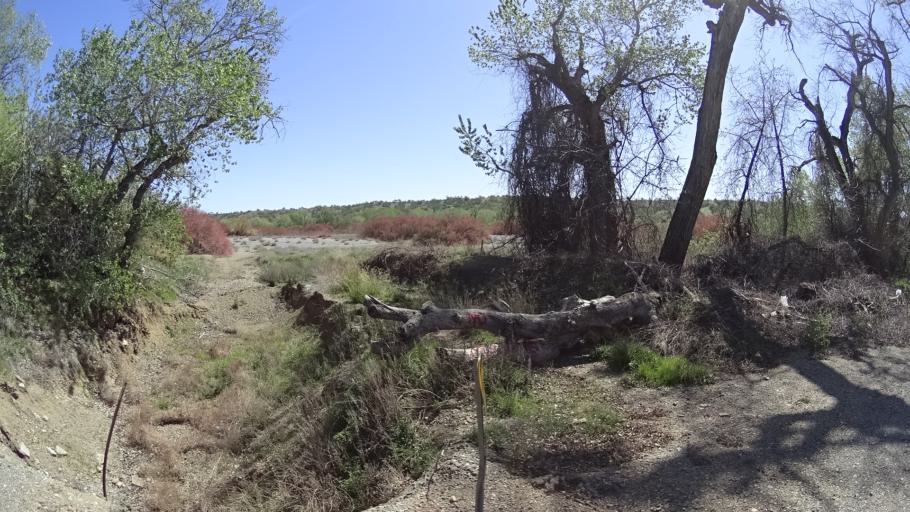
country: US
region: California
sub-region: Glenn County
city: Orland
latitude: 39.7382
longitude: -122.4102
